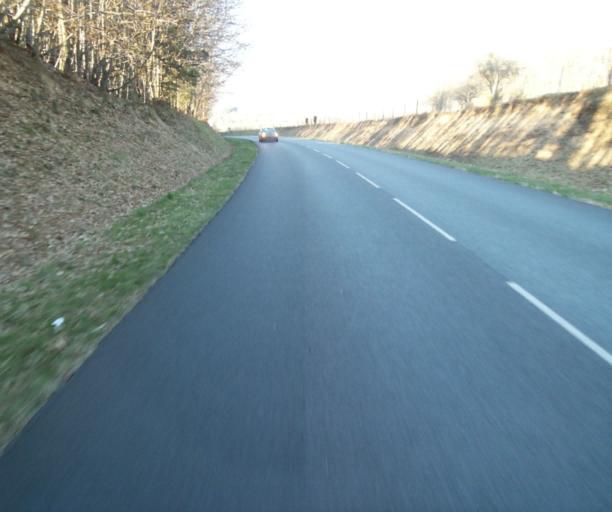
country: FR
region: Limousin
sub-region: Departement de la Correze
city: Seilhac
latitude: 45.3541
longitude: 1.7080
